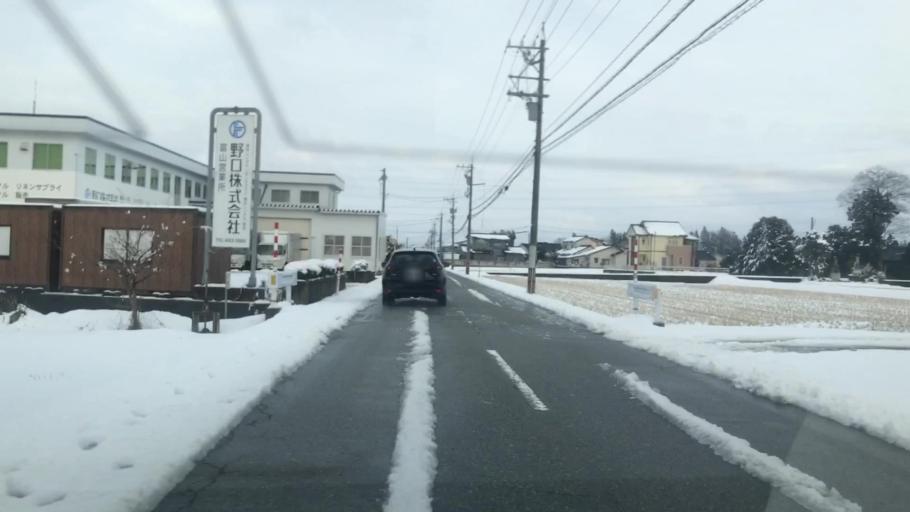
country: JP
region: Toyama
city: Toyama-shi
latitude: 36.6634
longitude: 137.2596
